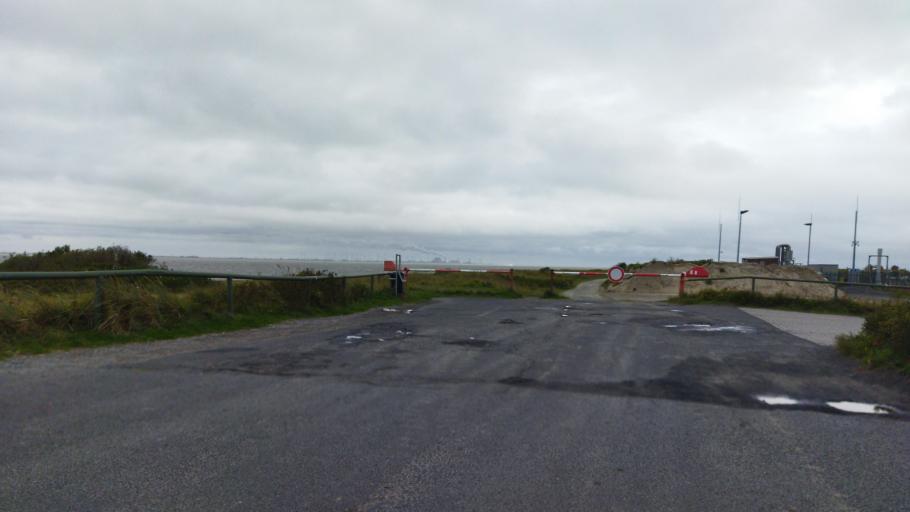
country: NL
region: Groningen
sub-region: Gemeente Delfzijl
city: Delfzijl
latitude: 53.3578
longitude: 7.0025
